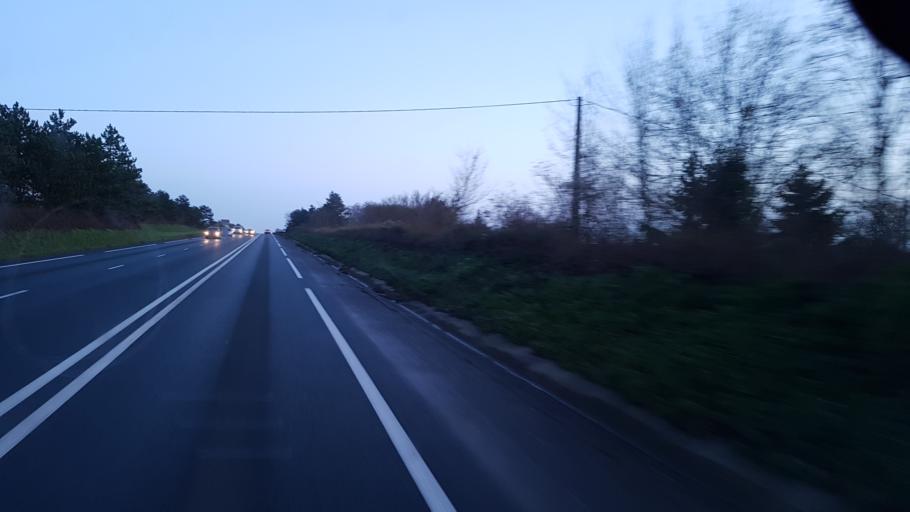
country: FR
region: Nord-Pas-de-Calais
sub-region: Departement du Nord
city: Lambres-lez-Douai
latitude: 50.3510
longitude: 3.0593
